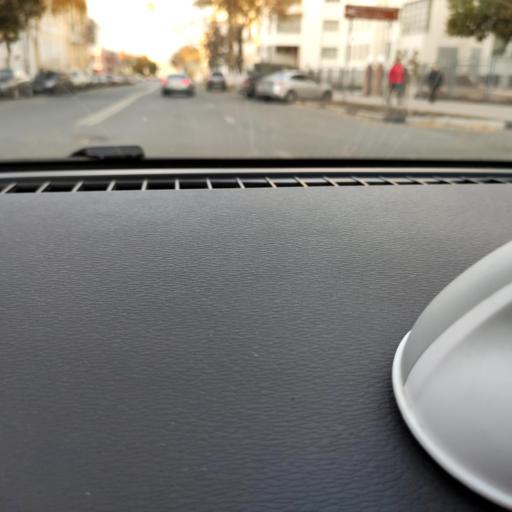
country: RU
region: Samara
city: Samara
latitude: 53.1956
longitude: 50.0971
